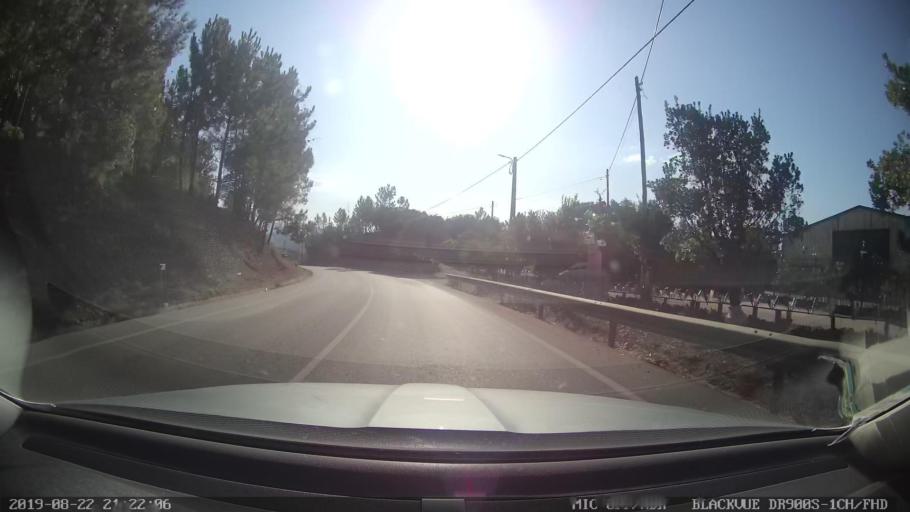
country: PT
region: Castelo Branco
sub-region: Serta
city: Serta
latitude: 39.8199
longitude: -8.1049
